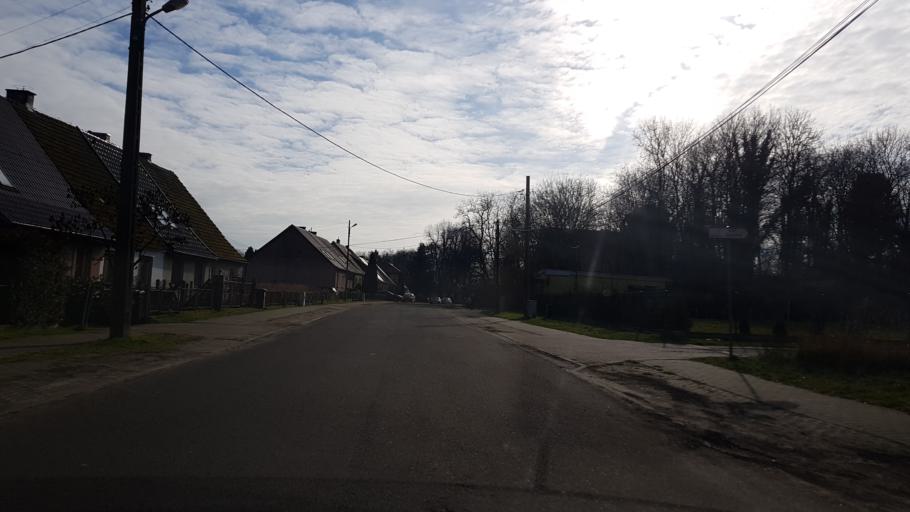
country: PL
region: West Pomeranian Voivodeship
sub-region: Powiat policki
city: Dobra
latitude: 53.5589
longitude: 14.3153
